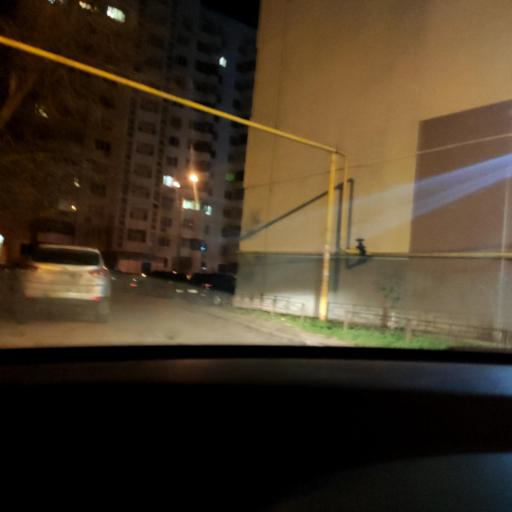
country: RU
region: Samara
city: Samara
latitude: 53.1884
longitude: 50.1440
